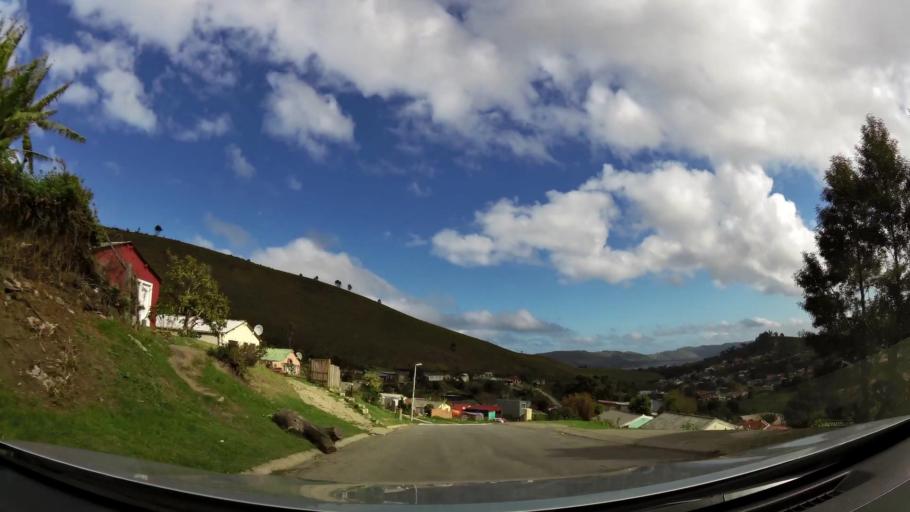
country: ZA
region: Western Cape
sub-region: Eden District Municipality
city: Knysna
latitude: -34.0541
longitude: 23.1043
